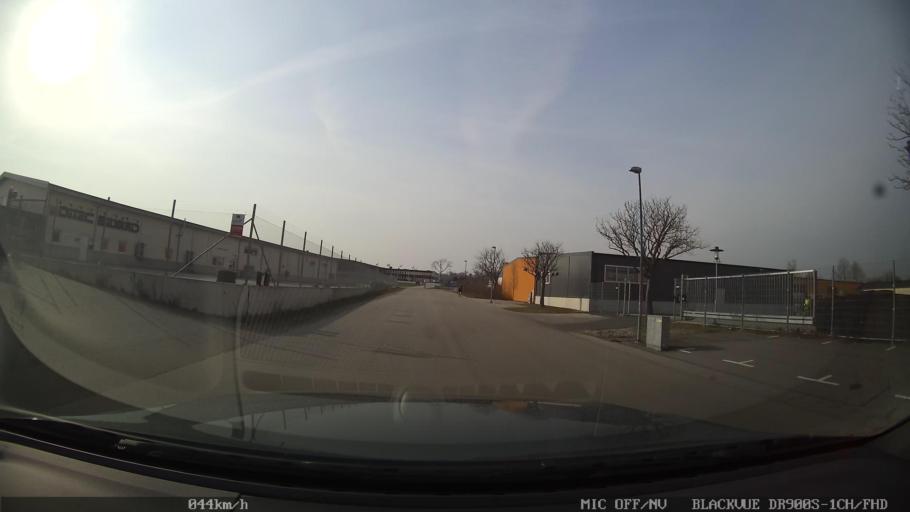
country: SE
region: Skane
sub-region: Ystads Kommun
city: Ystad
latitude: 55.4485
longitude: 13.8483
